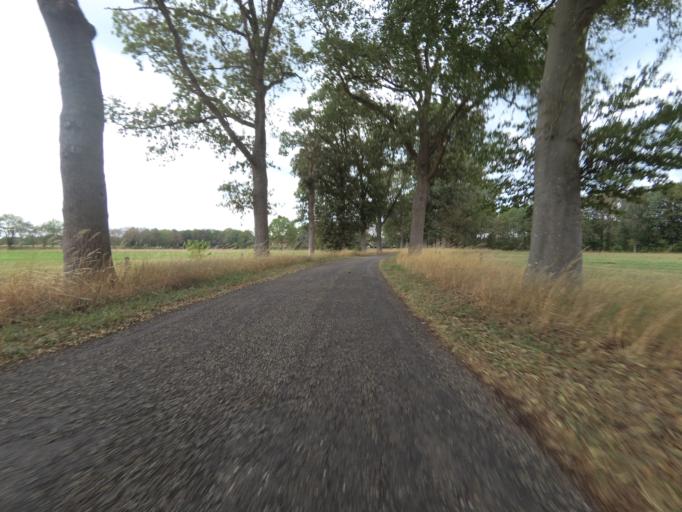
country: NL
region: Overijssel
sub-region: Gemeente Haaksbergen
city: Haaksbergen
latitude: 52.1855
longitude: 6.7568
